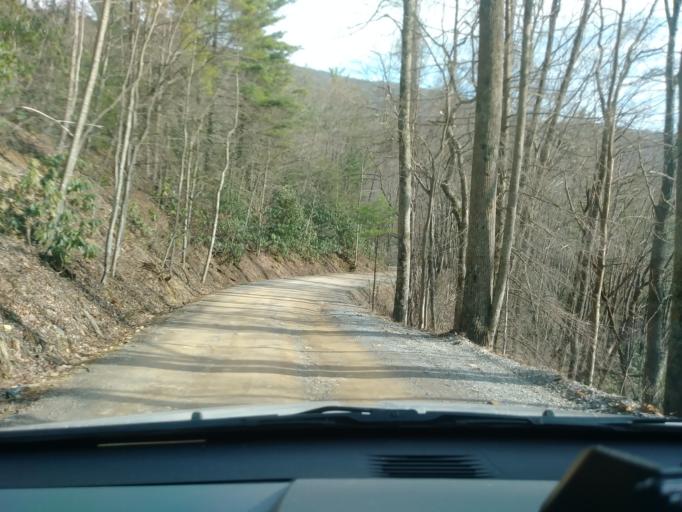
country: US
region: Tennessee
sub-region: Greene County
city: Tusculum
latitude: 36.0317
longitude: -82.7259
